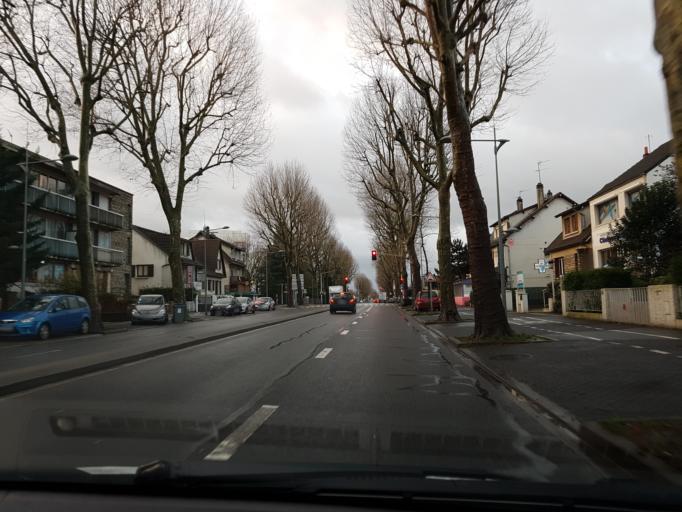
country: FR
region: Ile-de-France
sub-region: Departement du Val-de-Marne
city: L'Hay-les-Roses
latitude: 48.7719
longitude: 2.3389
